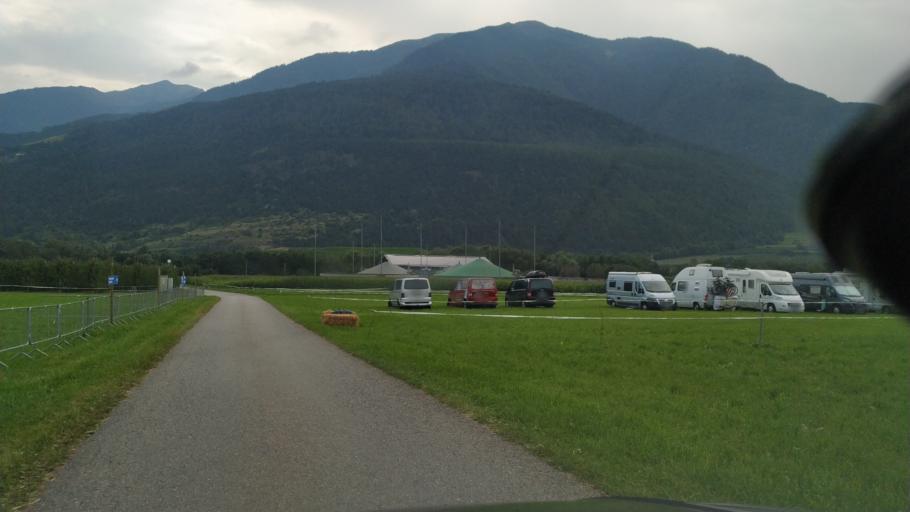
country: IT
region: Trentino-Alto Adige
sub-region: Bolzano
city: Sluderno
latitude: 46.6617
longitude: 10.5726
